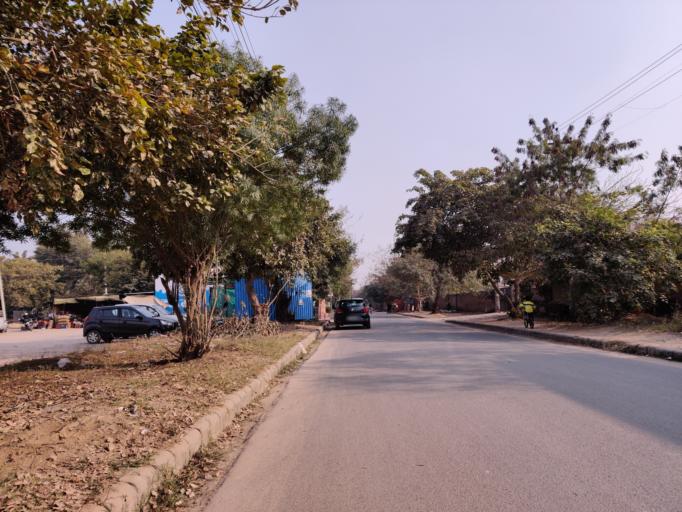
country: IN
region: Haryana
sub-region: Gurgaon
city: Gurgaon
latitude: 28.4420
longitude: 77.0658
